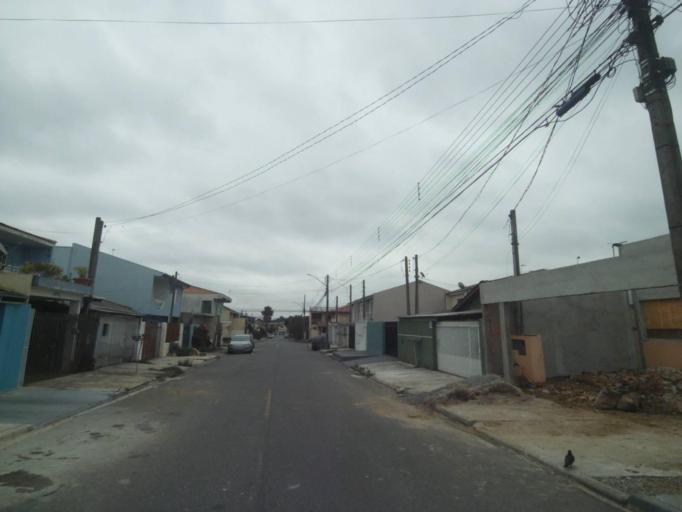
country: BR
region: Parana
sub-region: Araucaria
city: Araucaria
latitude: -25.5466
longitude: -49.3375
